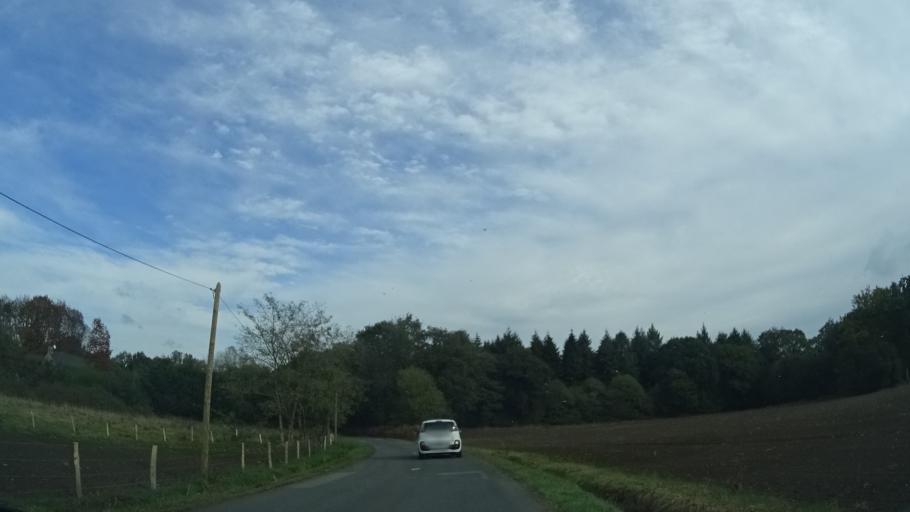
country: FR
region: Brittany
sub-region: Departement d'Ille-et-Vilaine
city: Bonnemain
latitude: 48.4541
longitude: -1.7952
